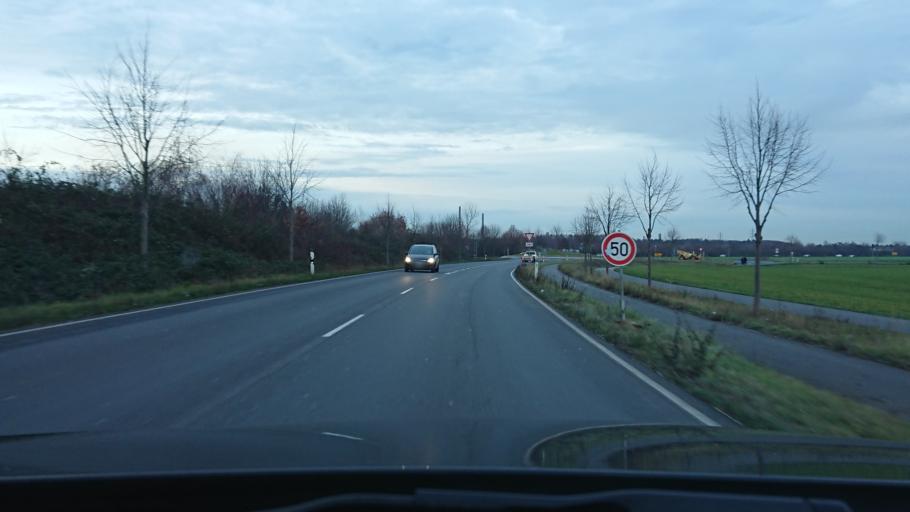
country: DE
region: North Rhine-Westphalia
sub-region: Regierungsbezirk Koln
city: Sinnersdorf
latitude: 51.0481
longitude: 6.8403
